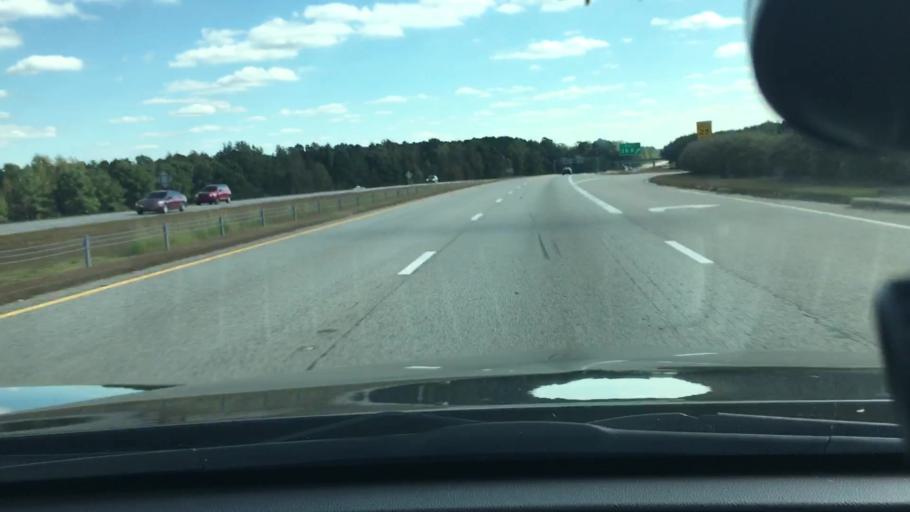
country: US
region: North Carolina
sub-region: Wilson County
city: Lucama
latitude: 35.7333
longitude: -78.0112
